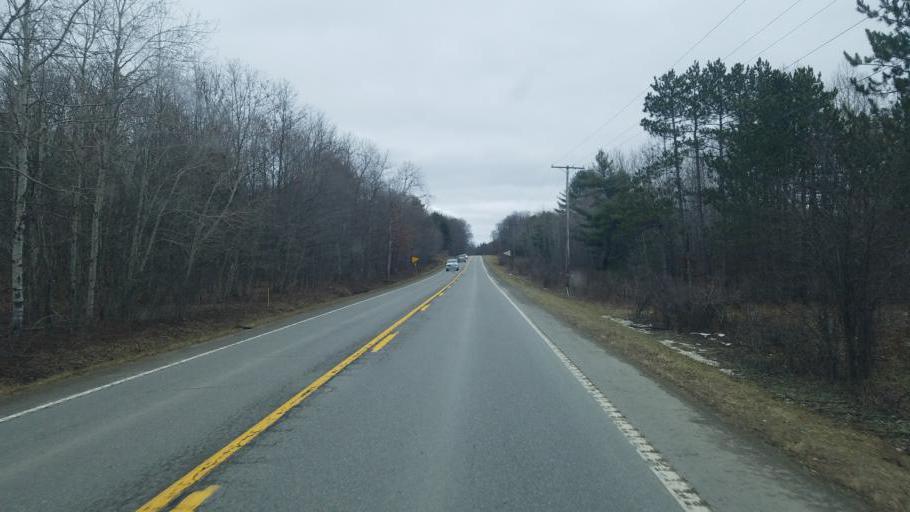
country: US
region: Pennsylvania
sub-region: Forest County
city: Marienville
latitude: 41.4268
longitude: -79.1974
